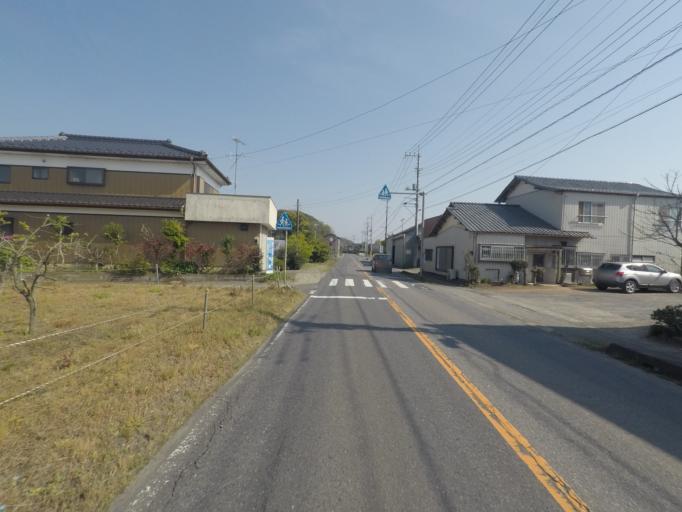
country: JP
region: Ibaraki
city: Itako
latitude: 36.0414
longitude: 140.4547
